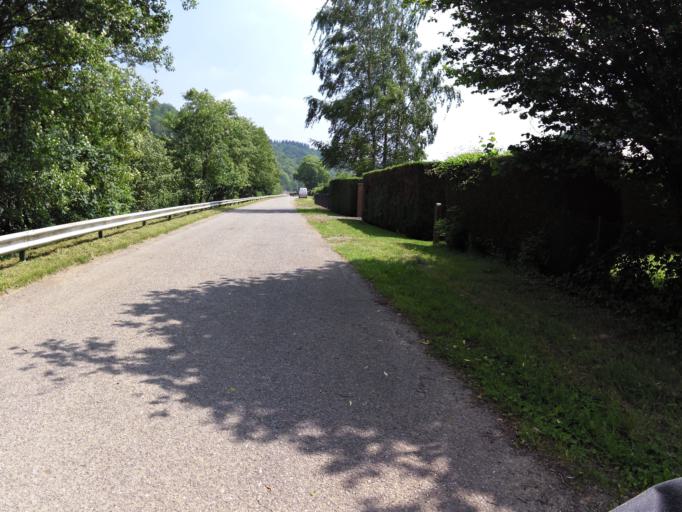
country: BE
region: Wallonia
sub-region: Province de Namur
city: Hastiere-Lavaux
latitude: 50.2134
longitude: 4.8425
